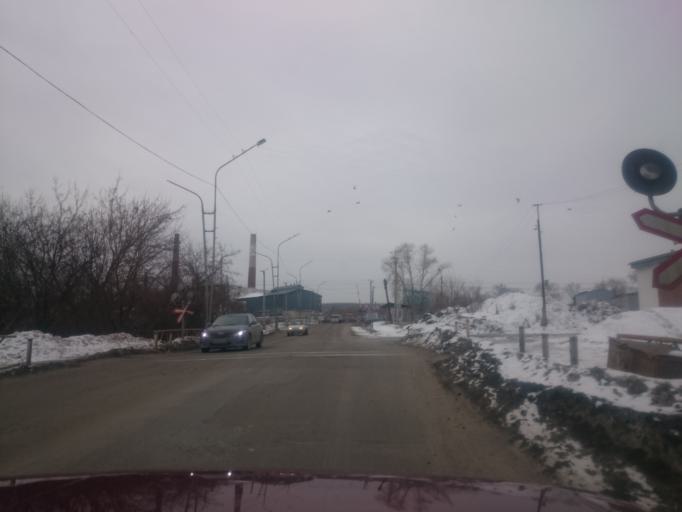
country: RU
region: Sverdlovsk
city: Irbit
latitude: 57.6667
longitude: 63.0597
